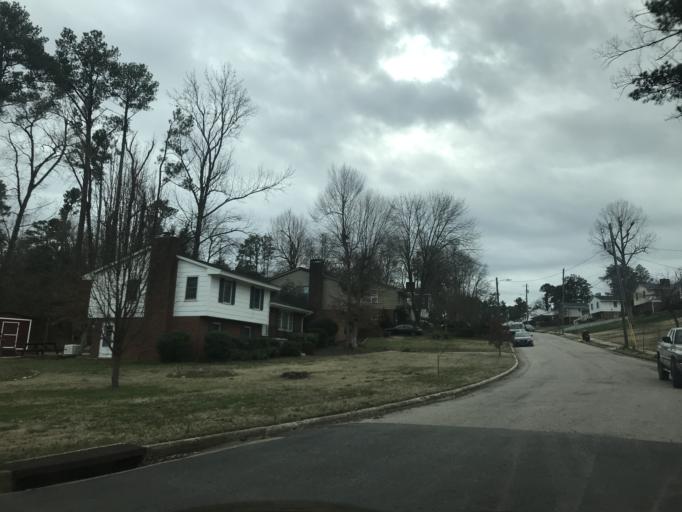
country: US
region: North Carolina
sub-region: Wake County
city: Raleigh
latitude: 35.7997
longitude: -78.6010
